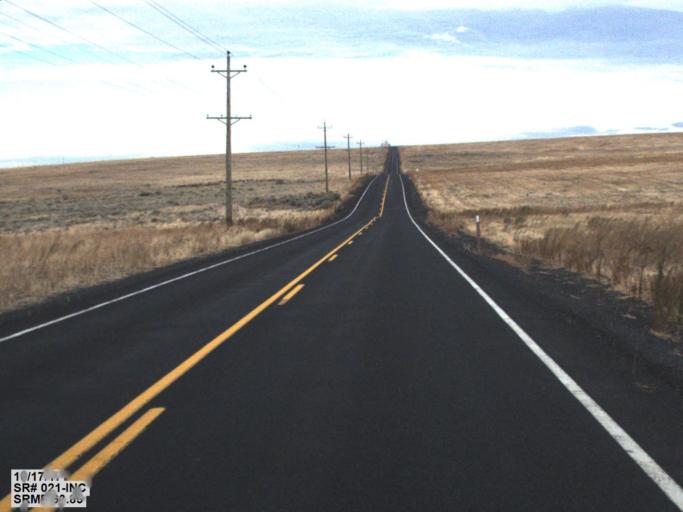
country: US
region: Washington
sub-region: Adams County
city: Ritzville
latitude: 47.4291
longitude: -118.7157
